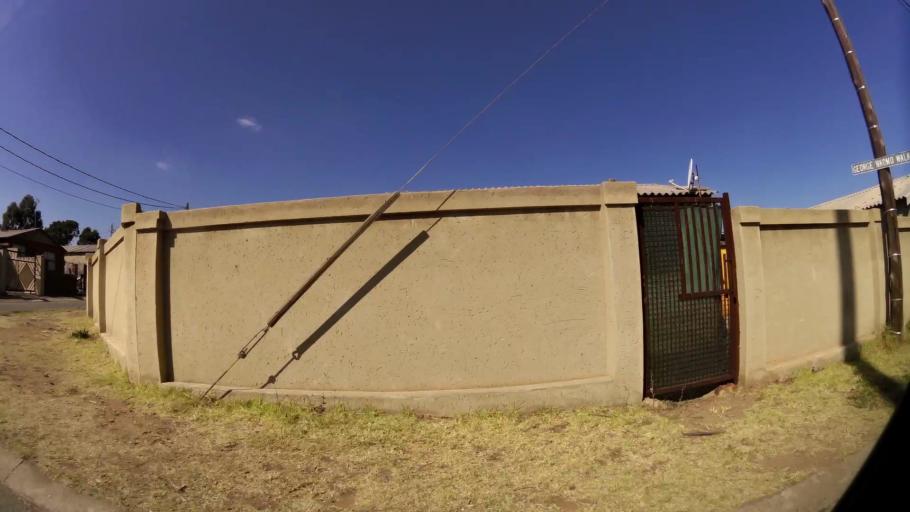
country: ZA
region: Gauteng
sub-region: City of Johannesburg Metropolitan Municipality
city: Soweto
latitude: -26.2268
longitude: 27.8868
